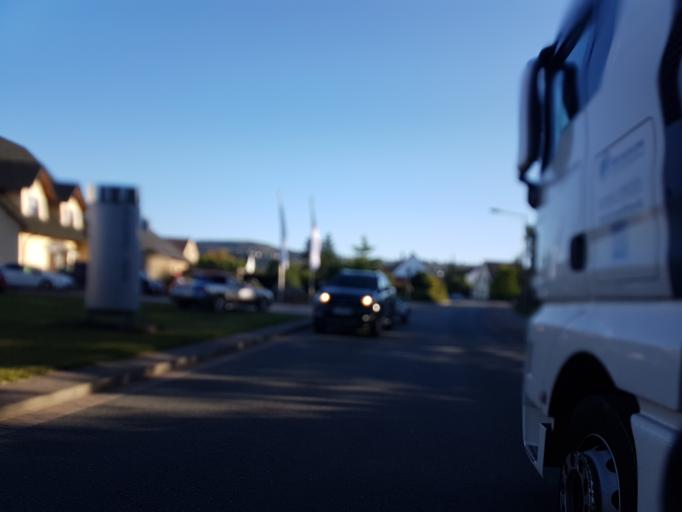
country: DE
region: North Rhine-Westphalia
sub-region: Regierungsbezirk Detmold
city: Vlotho
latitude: 52.1777
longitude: 8.8675
